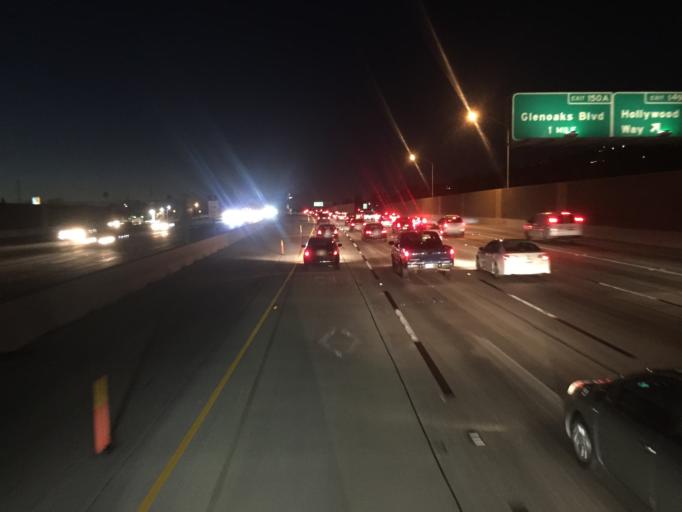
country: US
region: California
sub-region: Los Angeles County
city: Burbank
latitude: 34.2101
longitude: -118.3462
